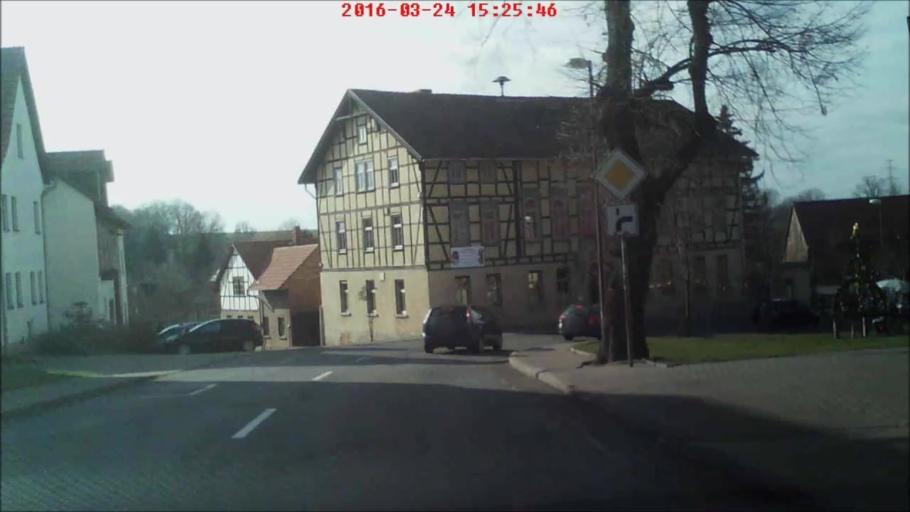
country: DE
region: Thuringia
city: Elxleben
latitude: 50.8650
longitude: 11.0568
